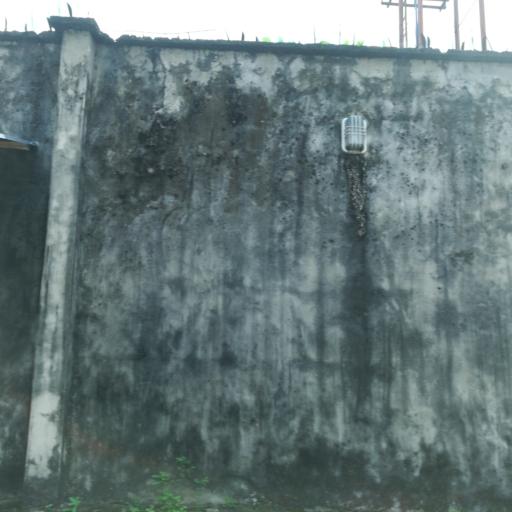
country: NG
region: Rivers
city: Port Harcourt
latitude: 4.7805
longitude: 7.0355
